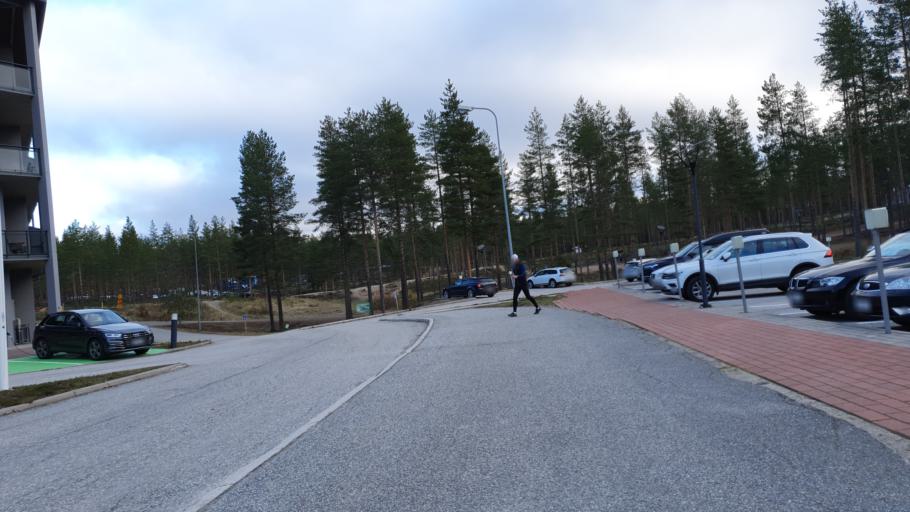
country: FI
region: Kainuu
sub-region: Kajaani
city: Vuokatti
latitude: 64.1407
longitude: 28.2954
